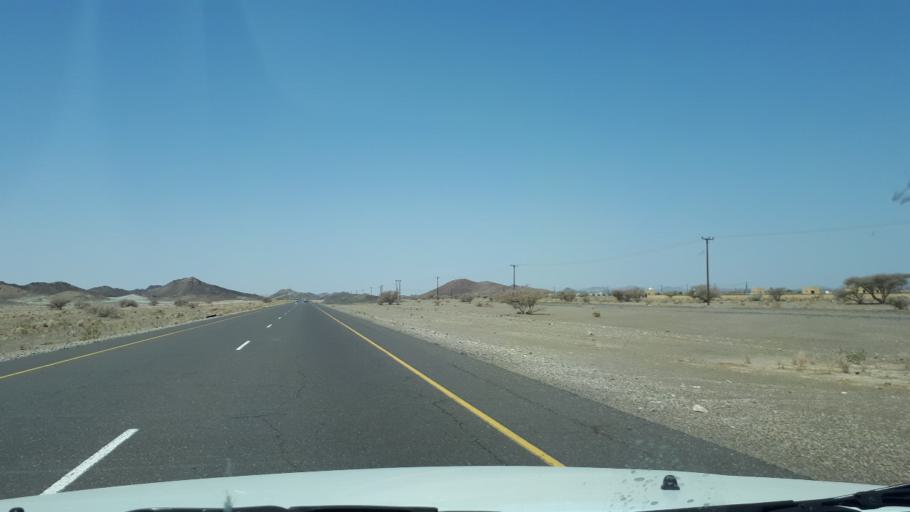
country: OM
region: Ash Sharqiyah
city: Ibra'
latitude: 22.6390
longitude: 58.4812
